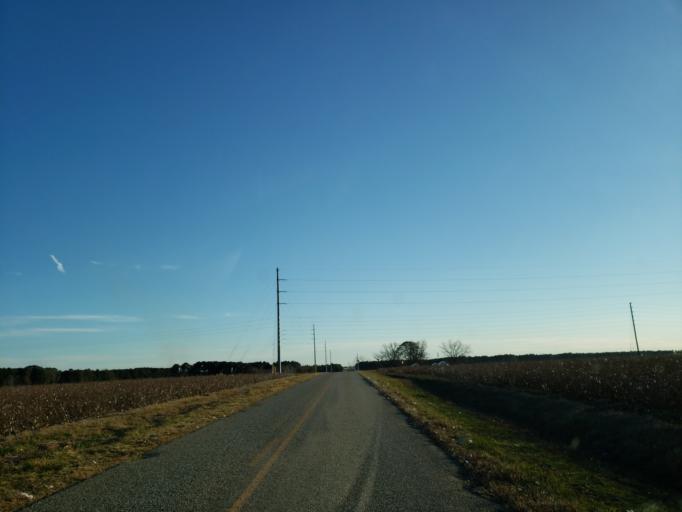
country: US
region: Georgia
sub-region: Dooly County
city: Vienna
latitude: 32.1456
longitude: -83.7610
